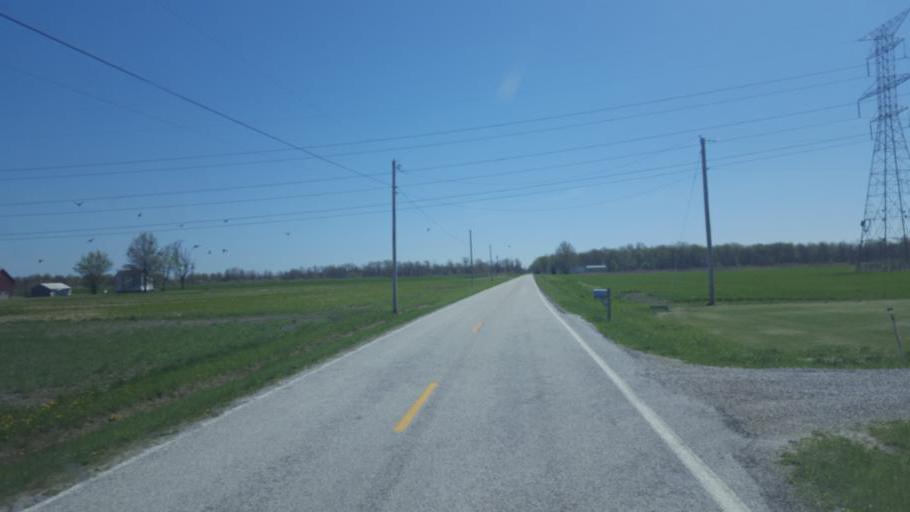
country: US
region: Ohio
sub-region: Ottawa County
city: Oak Harbor
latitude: 41.4970
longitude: -83.0734
